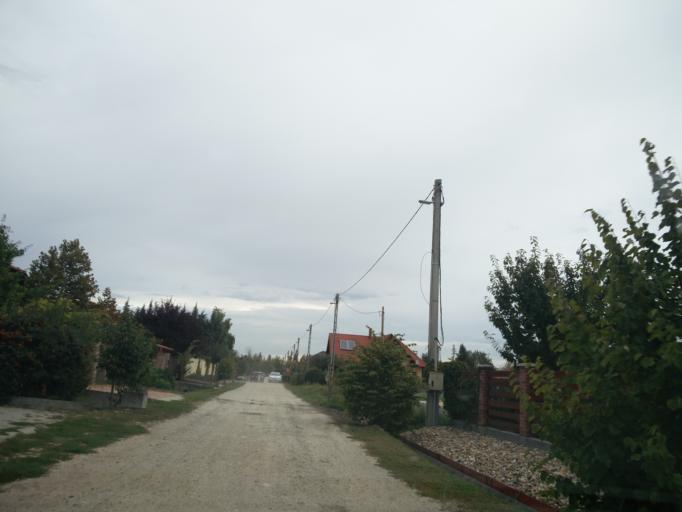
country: HU
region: Fejer
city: Gardony
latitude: 47.2149
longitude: 18.6365
